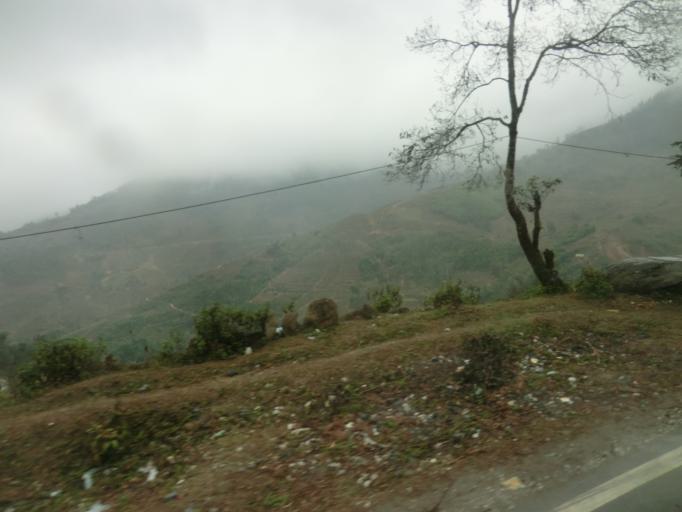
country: VN
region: Lao Cai
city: Sa Pa
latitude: 22.3965
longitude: 103.8872
